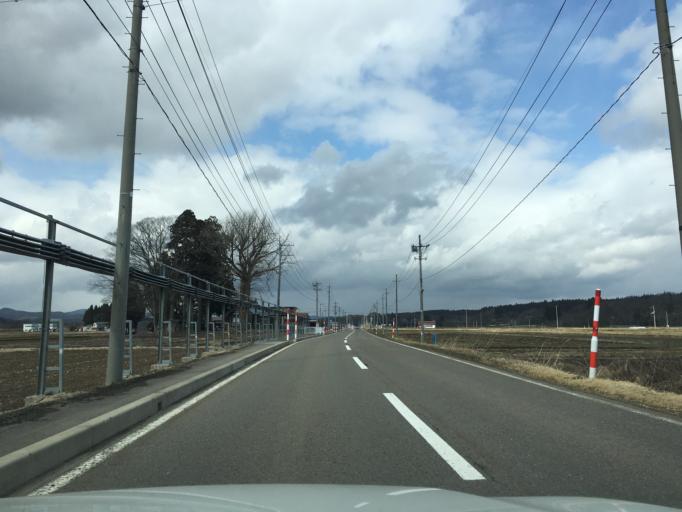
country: JP
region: Akita
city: Takanosu
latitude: 40.1337
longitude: 140.3564
